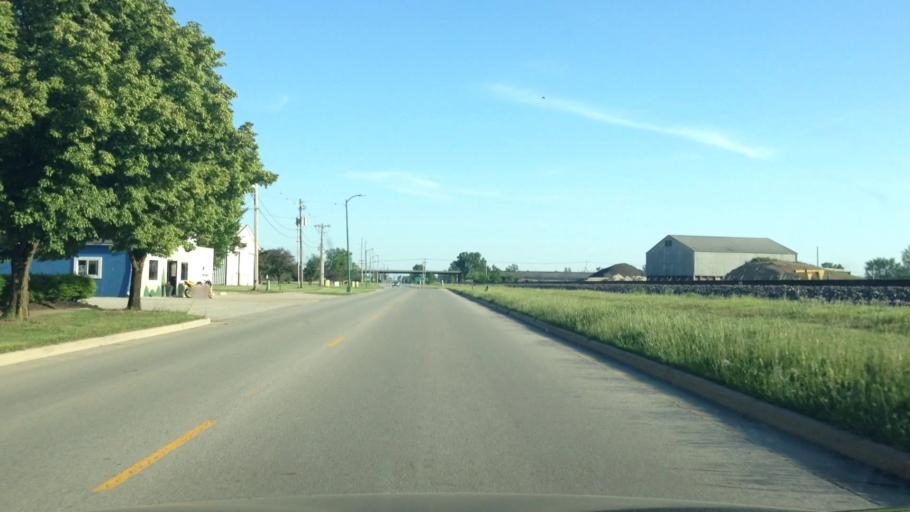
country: US
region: Ohio
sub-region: Auglaize County
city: Wapakoneta
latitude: 40.5621
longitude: -84.1944
